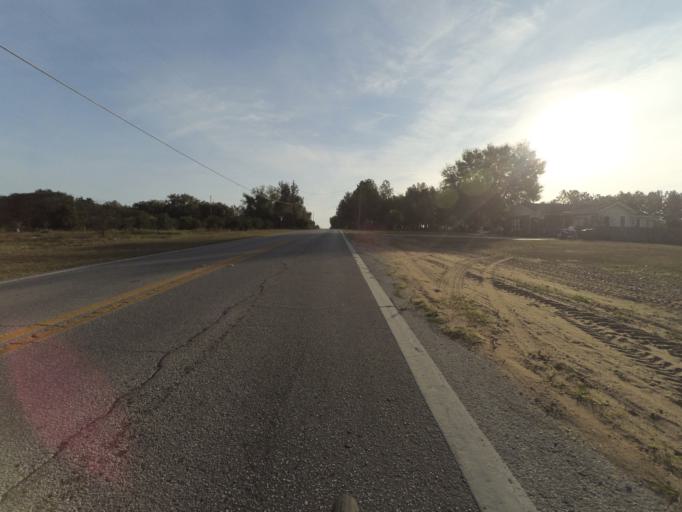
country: US
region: Florida
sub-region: Lake County
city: Umatilla
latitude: 28.9350
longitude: -81.6523
